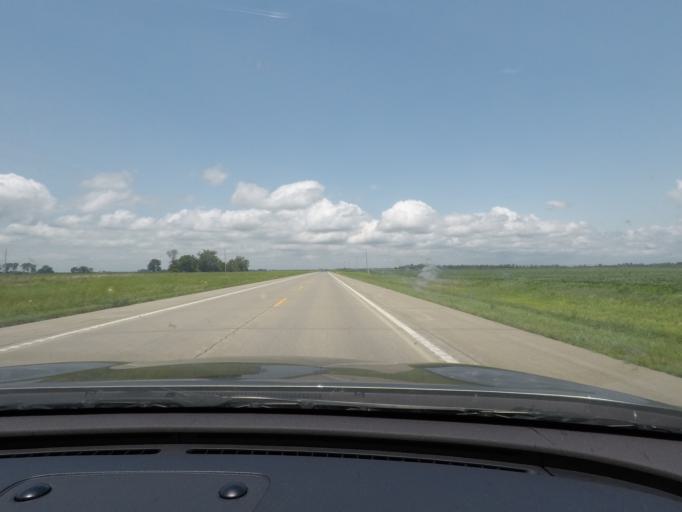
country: US
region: Missouri
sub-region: Carroll County
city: Carrollton
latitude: 39.2250
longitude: -93.5126
